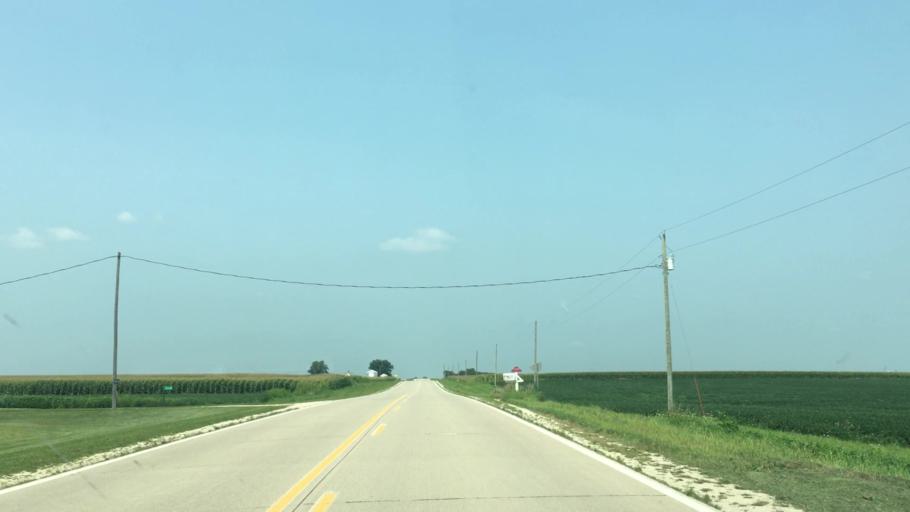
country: US
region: Iowa
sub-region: Fayette County
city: Oelwein
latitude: 42.7110
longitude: -91.8048
